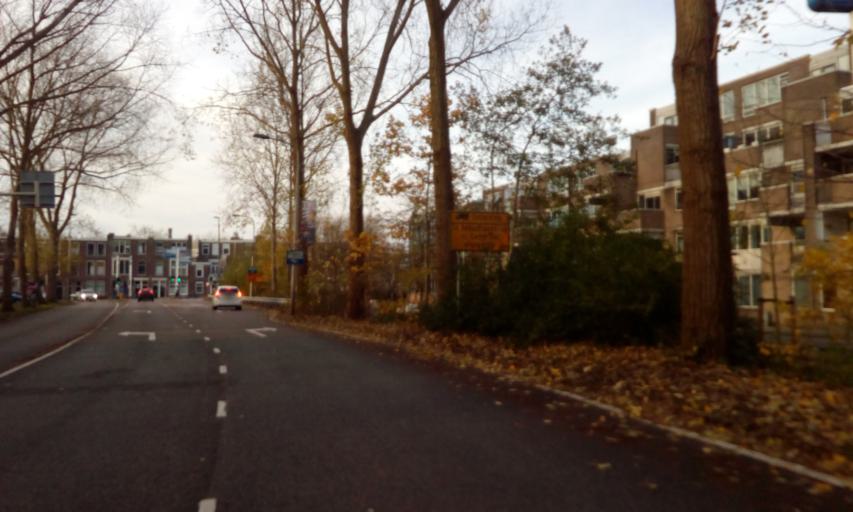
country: NL
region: South Holland
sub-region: Gemeente Delft
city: Delft
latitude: 52.0110
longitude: 4.3719
